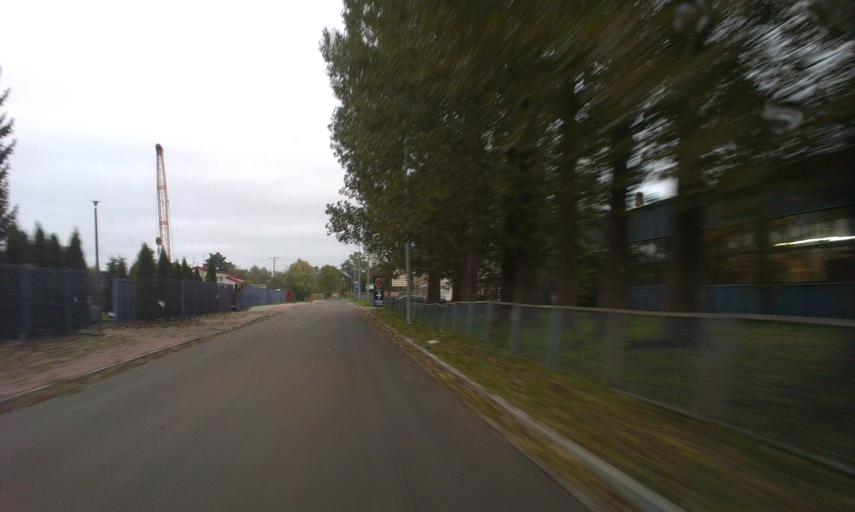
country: PL
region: West Pomeranian Voivodeship
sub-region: Powiat szczecinecki
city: Szczecinek
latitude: 53.7192
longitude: 16.6901
